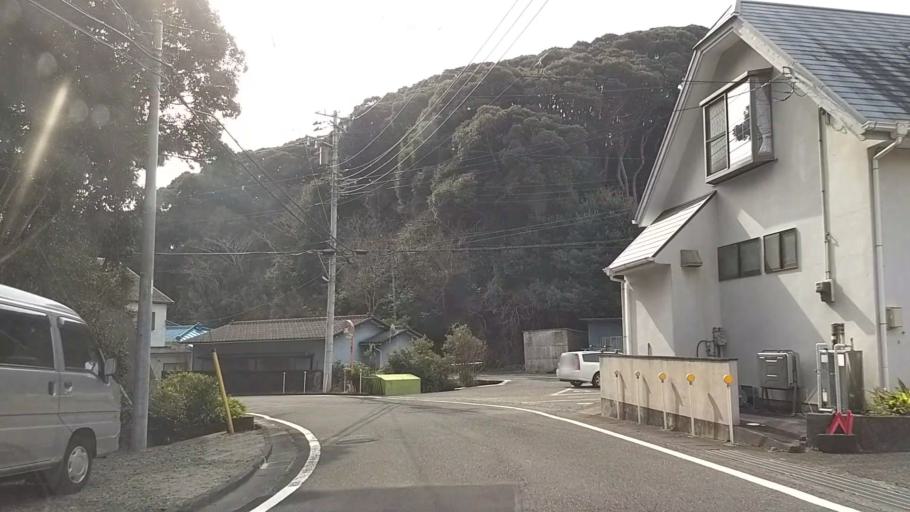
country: JP
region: Shizuoka
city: Shimoda
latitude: 34.6615
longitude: 138.9643
